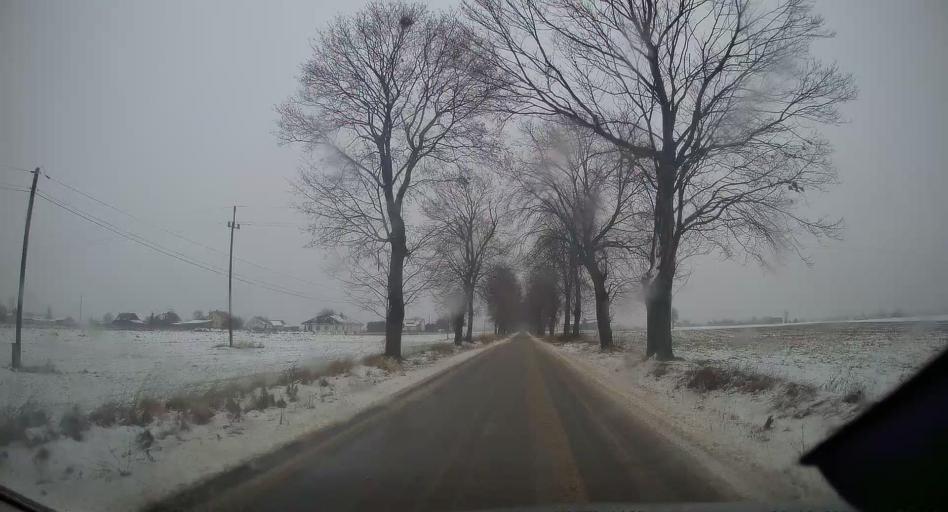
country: PL
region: Lodz Voivodeship
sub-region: Powiat tomaszowski
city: Czerniewice
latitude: 51.6801
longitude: 20.2188
